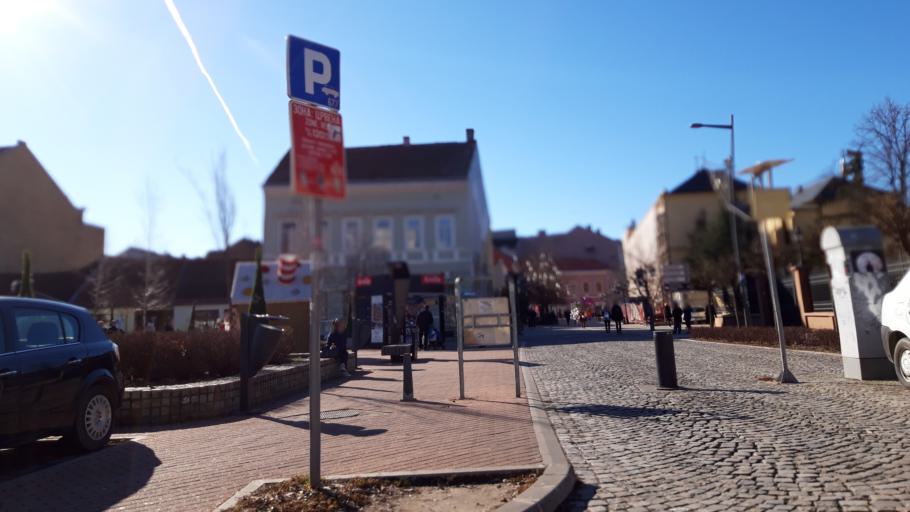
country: RS
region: Autonomna Pokrajina Vojvodina
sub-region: Juznobacki Okrug
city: Novi Sad
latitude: 45.2580
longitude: 19.8488
